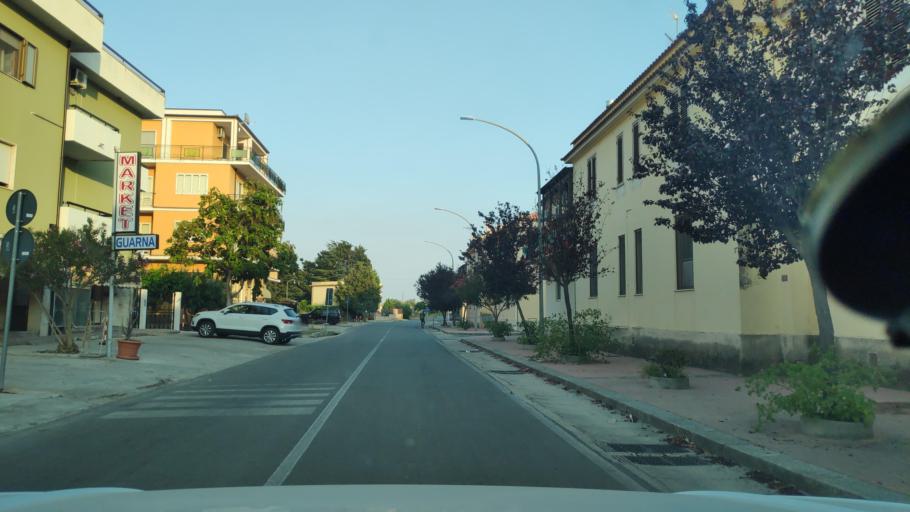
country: IT
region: Calabria
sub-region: Provincia di Catanzaro
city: Isca Marina
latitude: 38.6045
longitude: 16.5555
